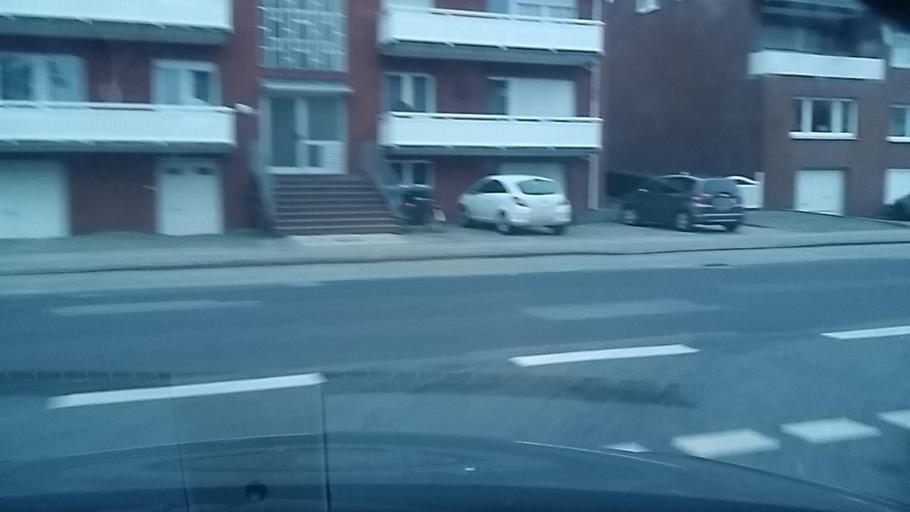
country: DE
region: Lower Saxony
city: Meppen
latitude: 52.7009
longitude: 7.2757
